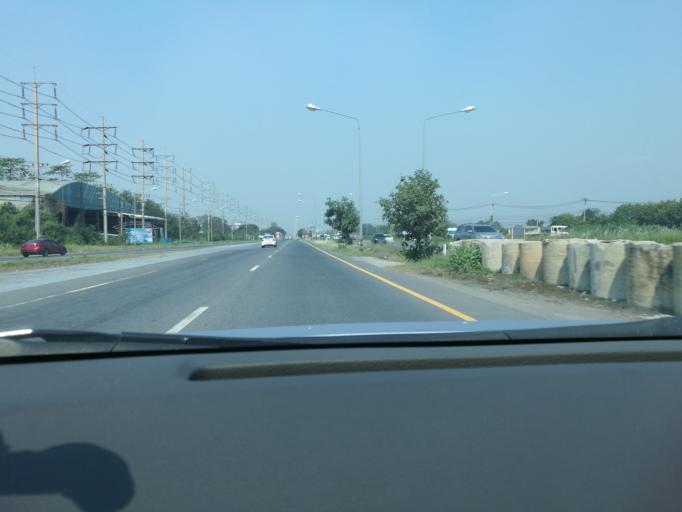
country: TH
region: Sara Buri
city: Saraburi
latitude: 14.5654
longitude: 100.9041
